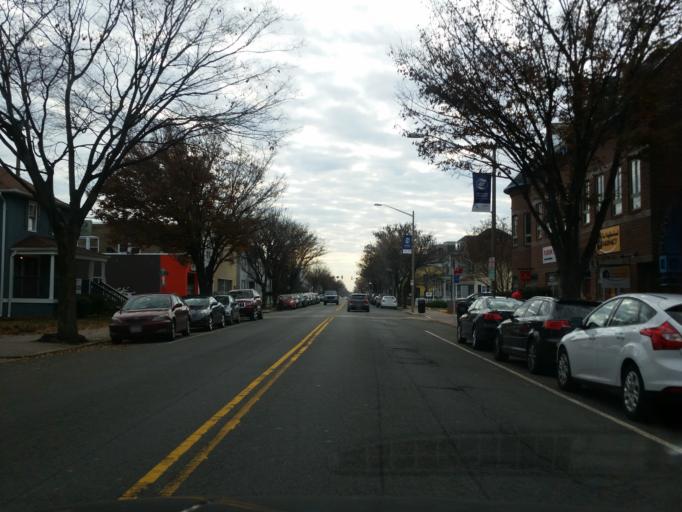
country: US
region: Virginia
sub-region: City of Alexandria
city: Alexandria
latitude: 38.8258
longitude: -77.0587
